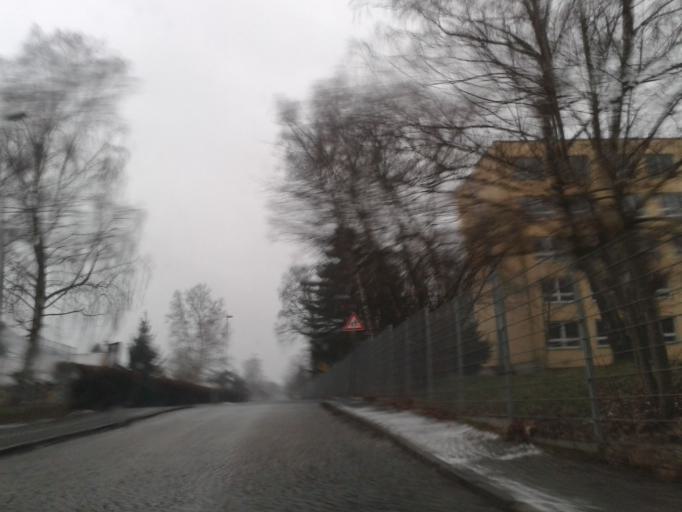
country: DE
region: Saxony
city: Radeberg
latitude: 51.1077
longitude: 13.9078
